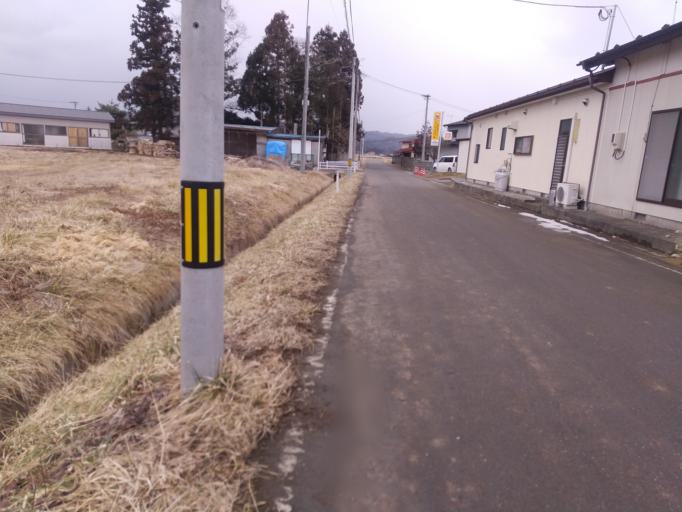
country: JP
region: Miyagi
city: Wakuya
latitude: 38.7006
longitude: 141.2657
